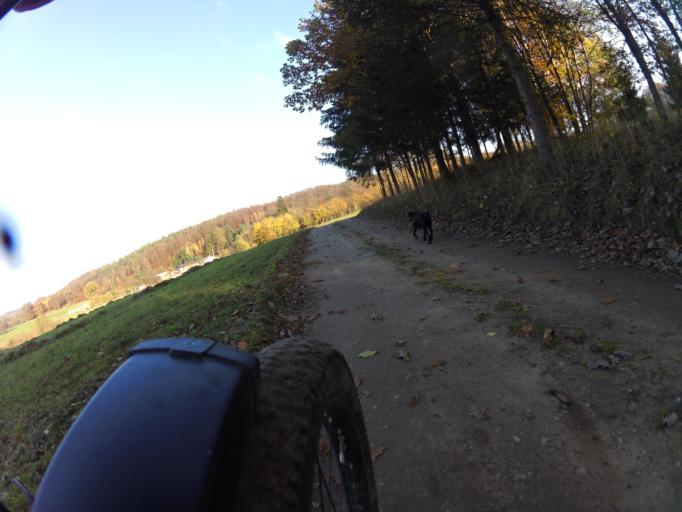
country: PL
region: Pomeranian Voivodeship
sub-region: Powiat pucki
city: Krokowa
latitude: 54.7453
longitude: 18.1925
